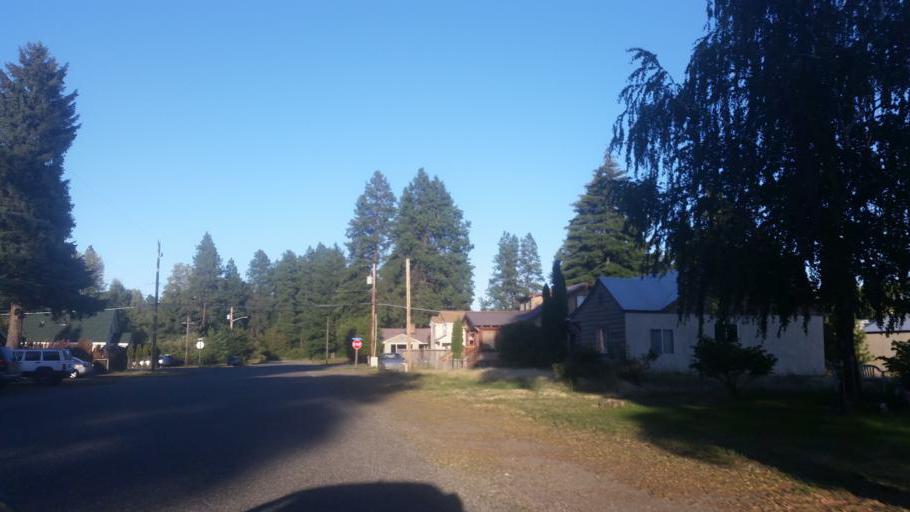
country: US
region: Washington
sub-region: Kittitas County
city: Cle Elum
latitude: 47.1870
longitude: -120.9494
